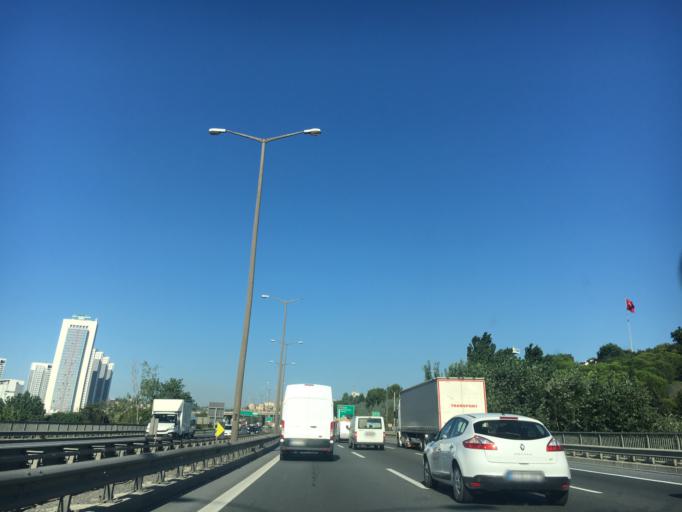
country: TR
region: Istanbul
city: Esenyurt
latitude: 41.0590
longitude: 28.6970
